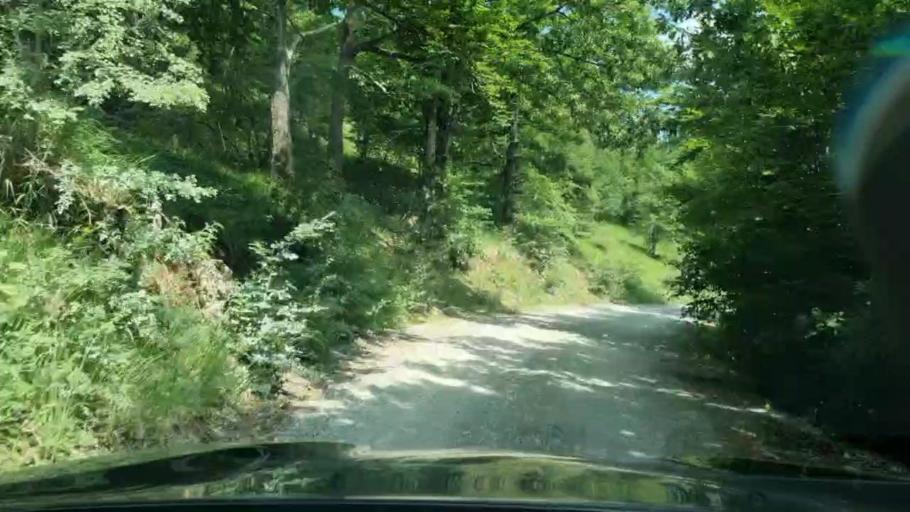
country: BA
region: Federation of Bosnia and Herzegovina
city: Bosansko Grahovo
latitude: 44.2984
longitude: 16.2714
